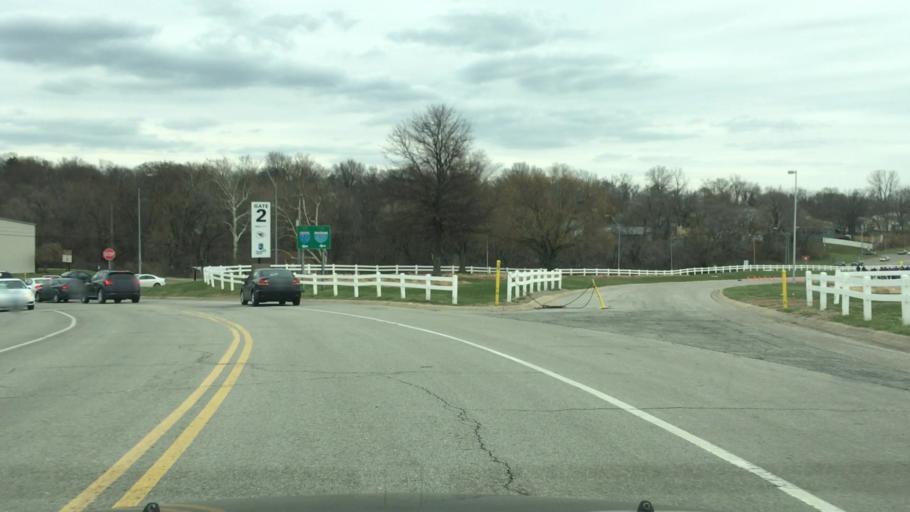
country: US
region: Missouri
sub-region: Jackson County
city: Raytown
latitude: 39.0471
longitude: -94.4766
